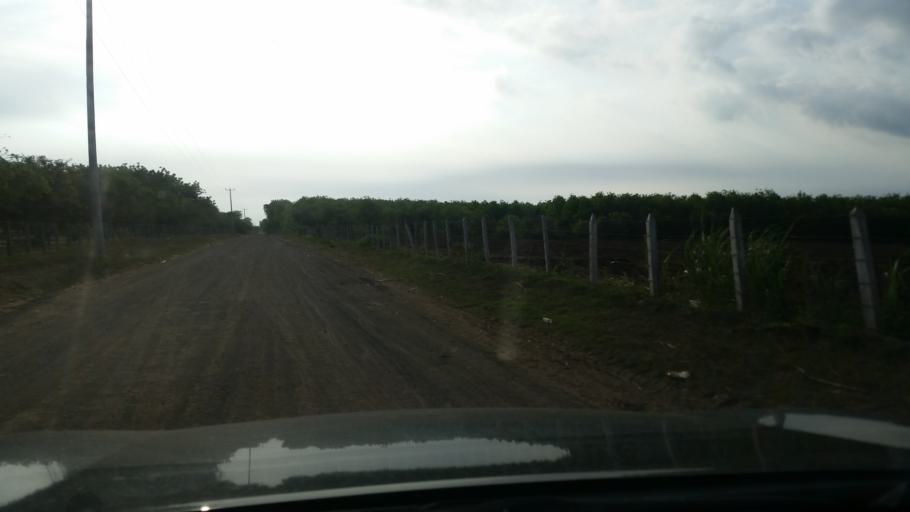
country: NI
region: Managua
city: Masachapa
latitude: 11.7678
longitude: -86.4871
